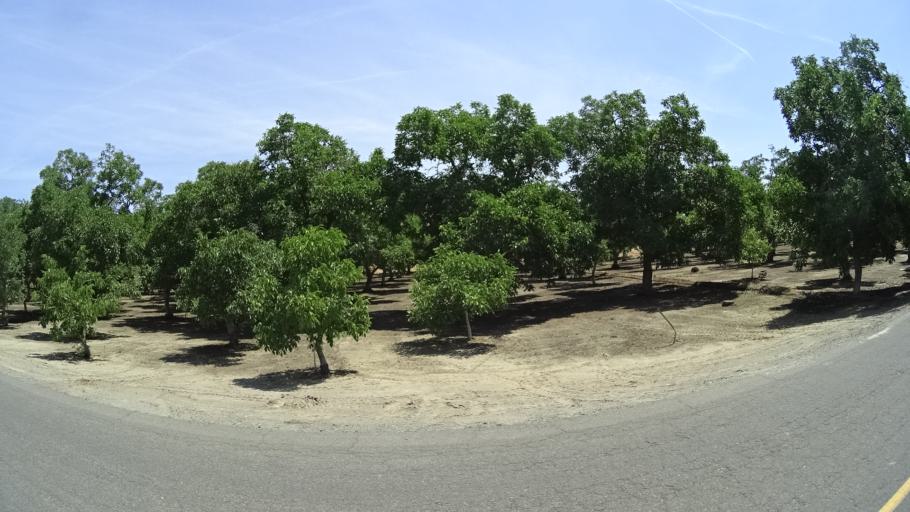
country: US
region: California
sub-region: Fresno County
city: Riverdale
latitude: 36.3977
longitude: -119.8094
